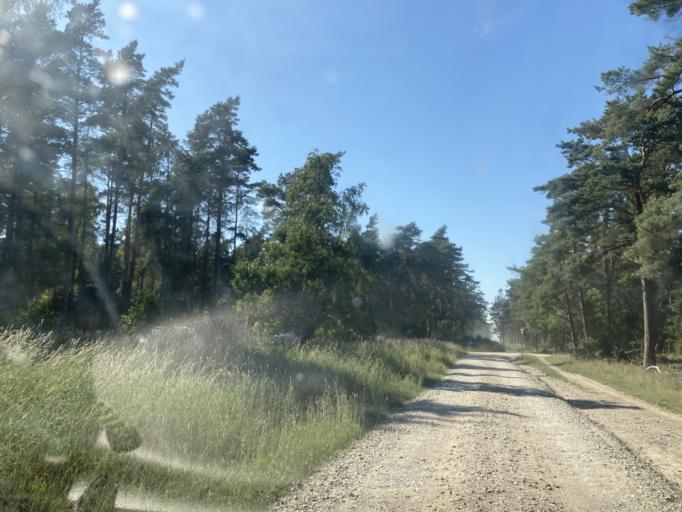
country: DK
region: Capital Region
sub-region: Halsnaes Kommune
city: Frederiksvaerk
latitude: 56.0185
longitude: 12.0089
